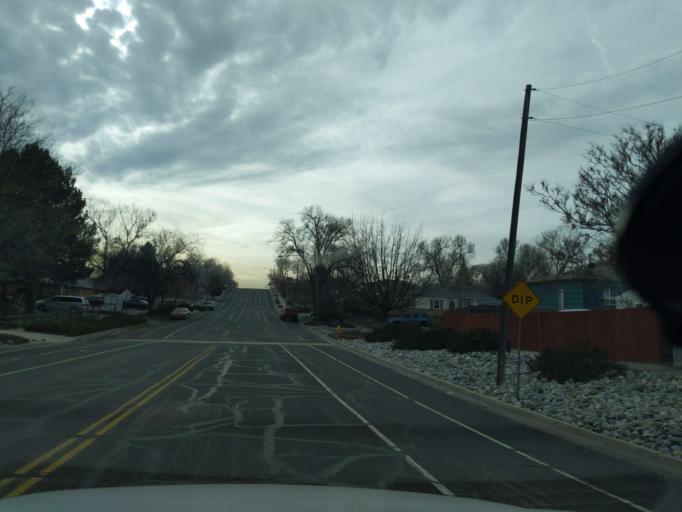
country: US
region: Colorado
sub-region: Adams County
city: Thornton
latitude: 39.8623
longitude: -104.9518
